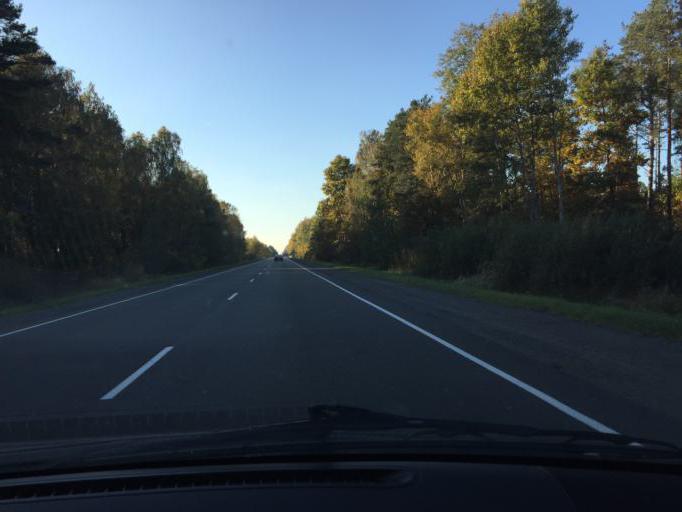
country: BY
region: Brest
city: Horad Luninyets
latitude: 52.3009
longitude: 26.7207
